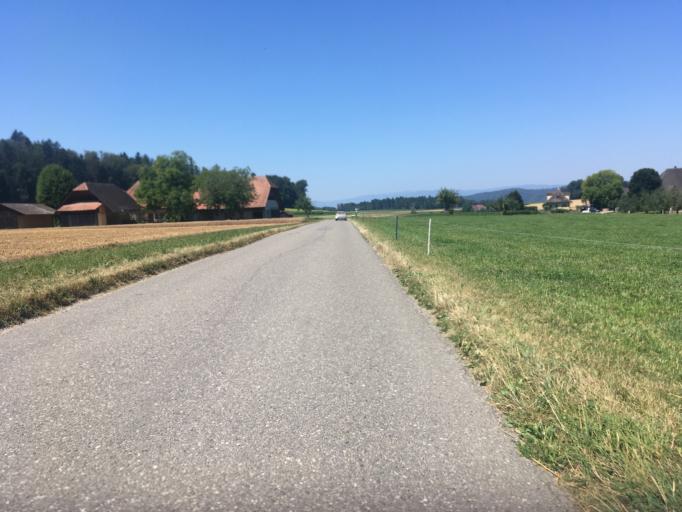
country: CH
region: Bern
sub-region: Bern-Mittelland District
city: Fraubrunnen
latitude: 47.0892
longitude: 7.4981
